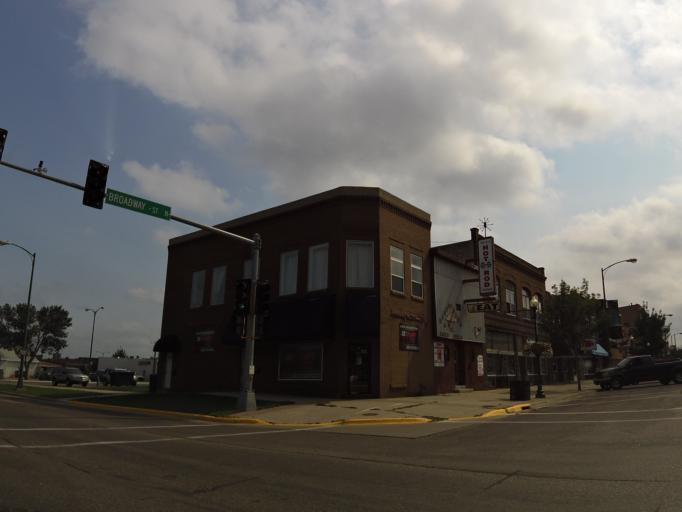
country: US
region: South Dakota
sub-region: Codington County
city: Watertown
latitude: 44.9018
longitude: -97.1140
